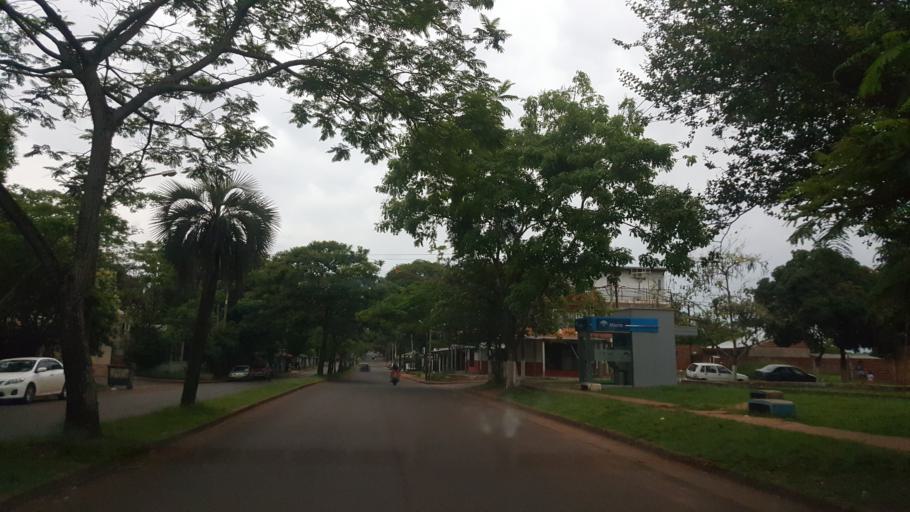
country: AR
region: Misiones
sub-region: Departamento de Capital
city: Posadas
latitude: -27.3582
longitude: -55.9305
